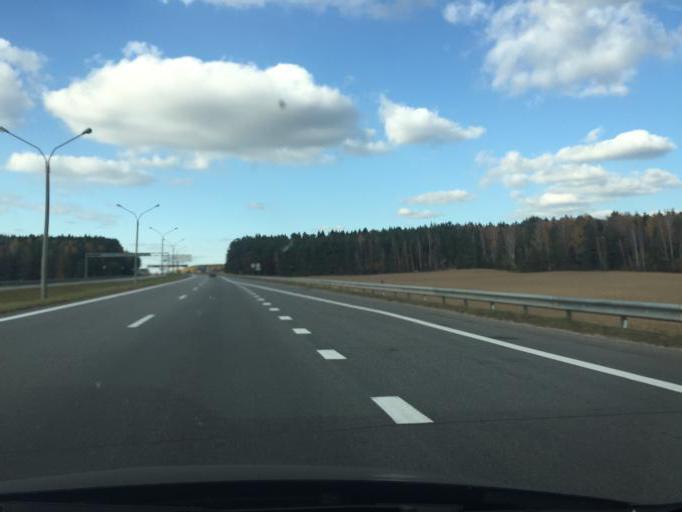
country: BY
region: Minsk
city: Slabada
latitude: 53.9550
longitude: 27.9720
